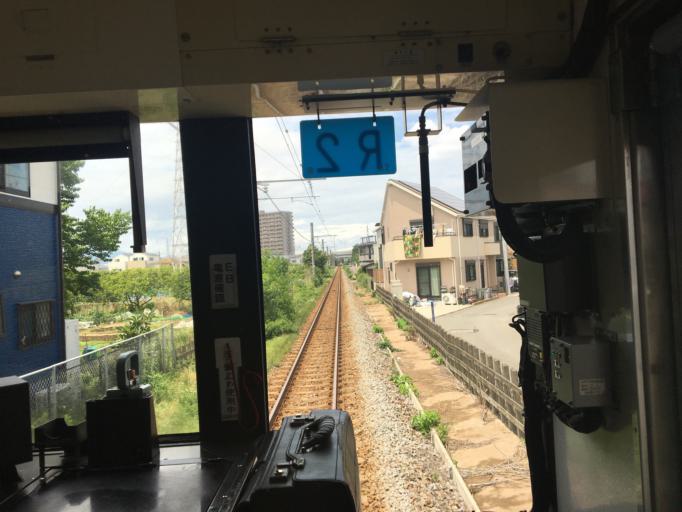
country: JP
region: Kanagawa
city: Chigasaki
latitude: 35.3468
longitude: 139.4035
